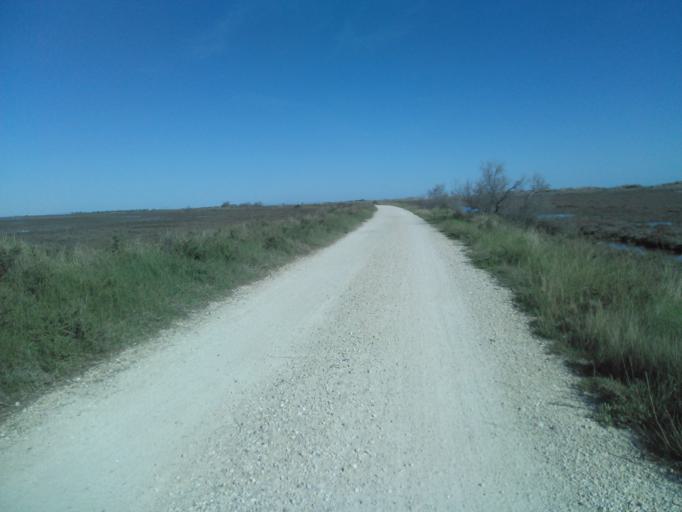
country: FR
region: Provence-Alpes-Cote d'Azur
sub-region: Departement des Bouches-du-Rhone
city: Saintes-Maries-de-la-Mer
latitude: 43.4613
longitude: 4.5006
